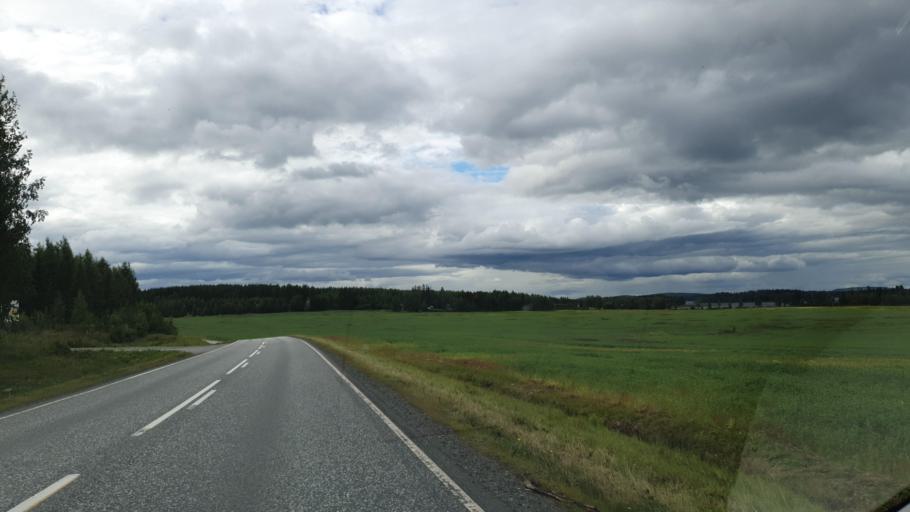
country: FI
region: Northern Savo
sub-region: Ylae-Savo
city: Iisalmi
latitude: 63.5205
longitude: 27.1944
